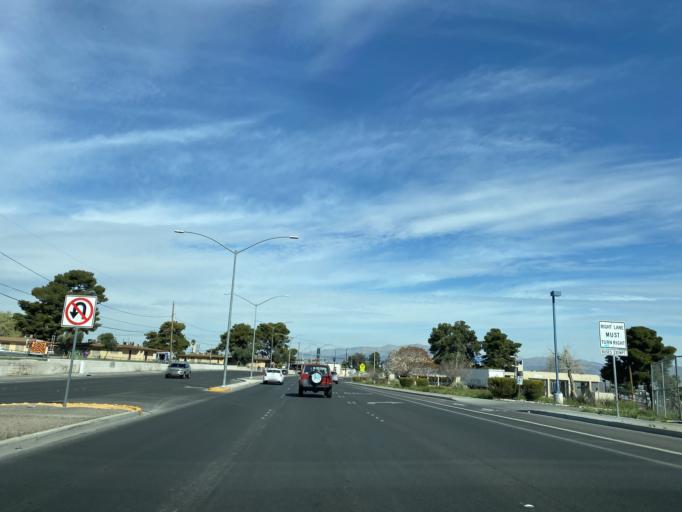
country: US
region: Nevada
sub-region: Clark County
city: Las Vegas
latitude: 36.1721
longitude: -115.1299
